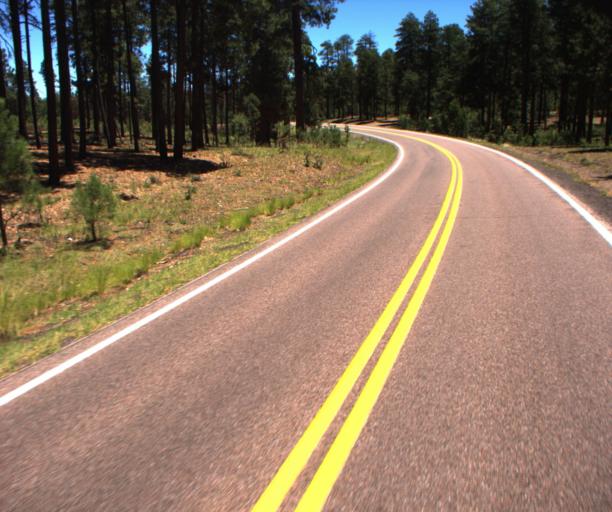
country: US
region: Arizona
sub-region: Gila County
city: Pine
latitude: 34.4414
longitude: -111.4567
